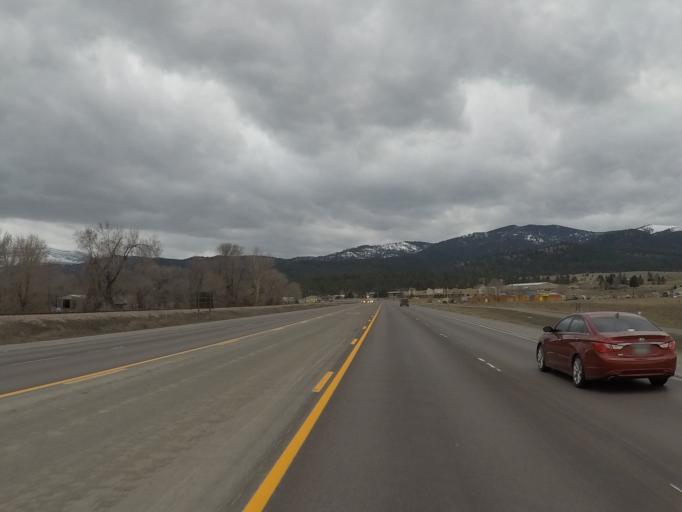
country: US
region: Montana
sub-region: Missoula County
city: Orchard Homes
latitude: 46.8271
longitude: -114.0683
